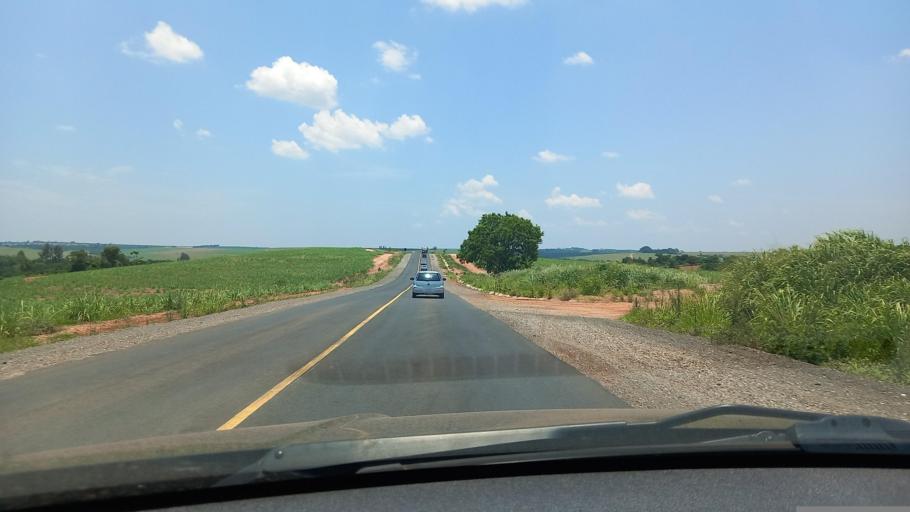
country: BR
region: Sao Paulo
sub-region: Moji-Guacu
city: Mogi-Gaucu
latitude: -22.3680
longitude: -46.8736
